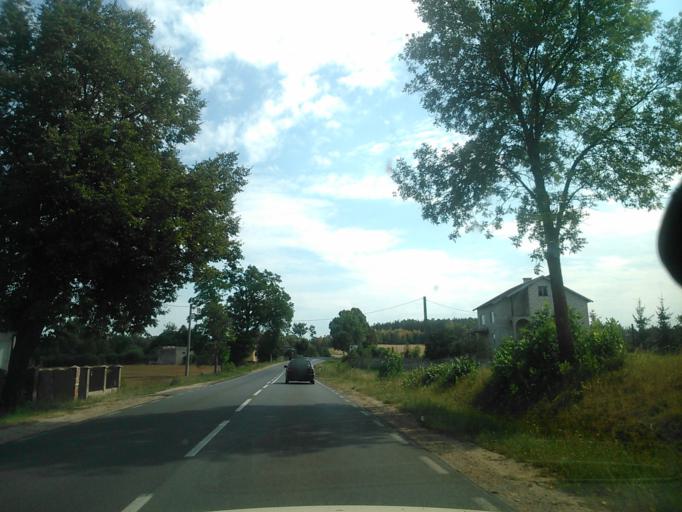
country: PL
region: Warmian-Masurian Voivodeship
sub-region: Powiat dzialdowski
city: Ilowo -Osada
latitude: 53.1528
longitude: 20.3216
